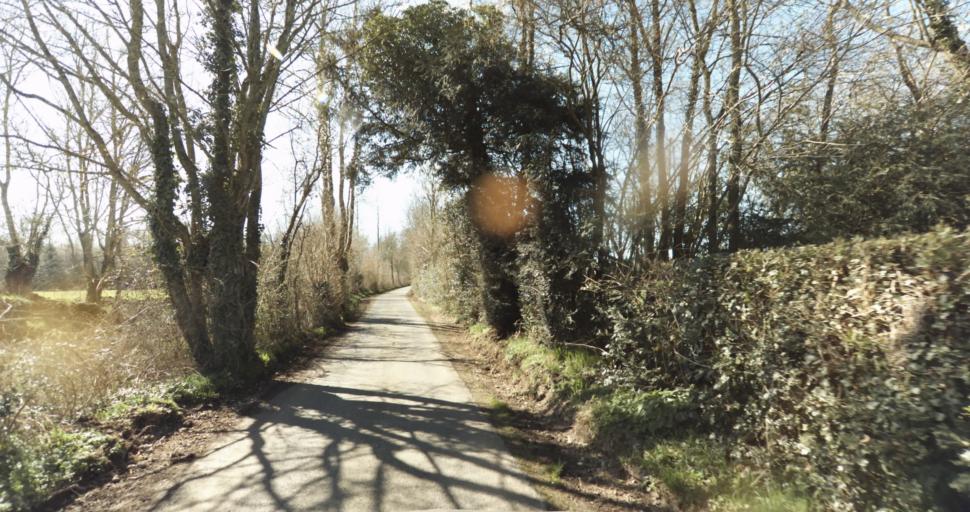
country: FR
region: Lower Normandy
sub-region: Departement du Calvados
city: Livarot
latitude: 48.9774
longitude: 0.0972
